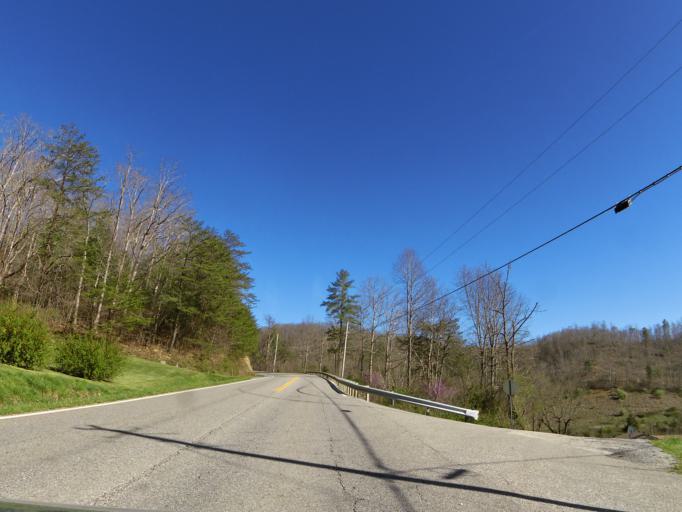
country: US
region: Tennessee
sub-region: Scott County
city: Huntsville
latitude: 36.4335
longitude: -84.4565
